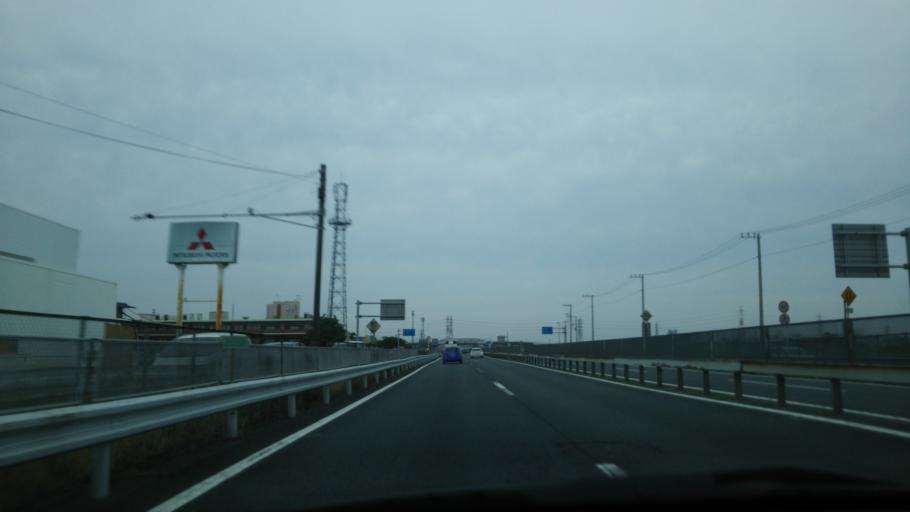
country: JP
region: Kanagawa
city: Isehara
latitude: 35.3860
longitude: 139.3313
